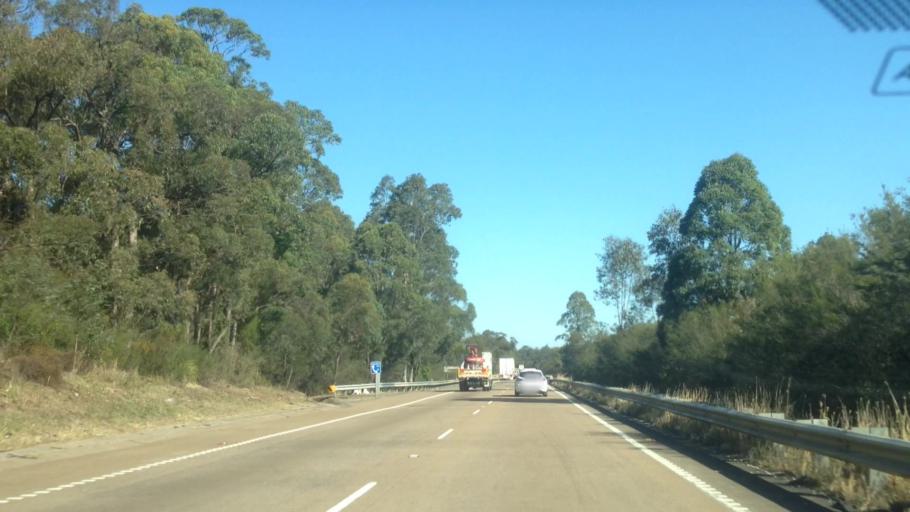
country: AU
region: New South Wales
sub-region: Wyong Shire
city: Charmhaven
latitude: -33.1641
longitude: 151.4689
